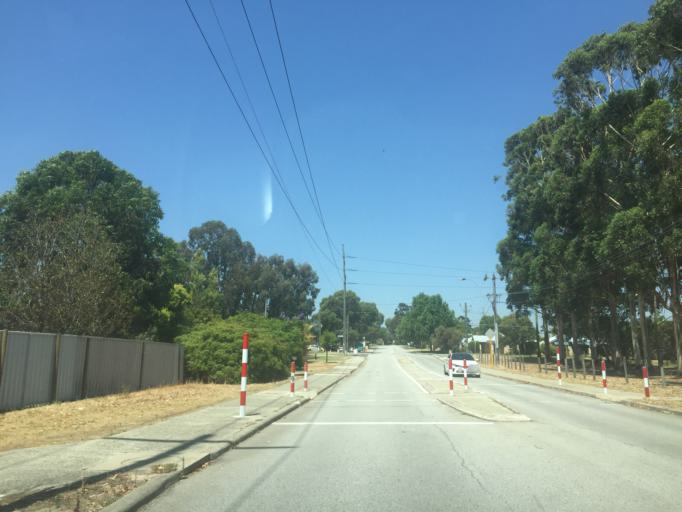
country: AU
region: Western Australia
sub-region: City of Cockburn
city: City of Cockburn
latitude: -32.0928
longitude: 115.8393
